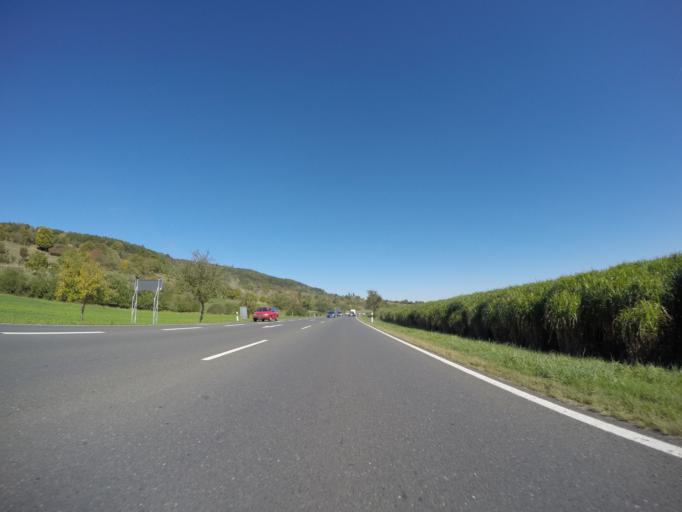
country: DE
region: Bavaria
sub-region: Upper Franconia
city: Kirchehrenbach
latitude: 49.7483
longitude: 11.1396
